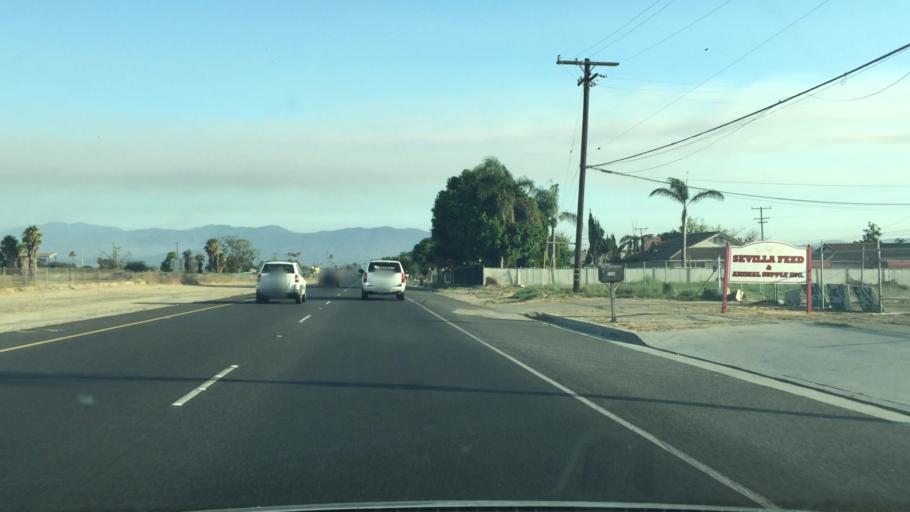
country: US
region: California
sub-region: San Bernardino County
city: Chino
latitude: 34.0177
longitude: -117.6509
